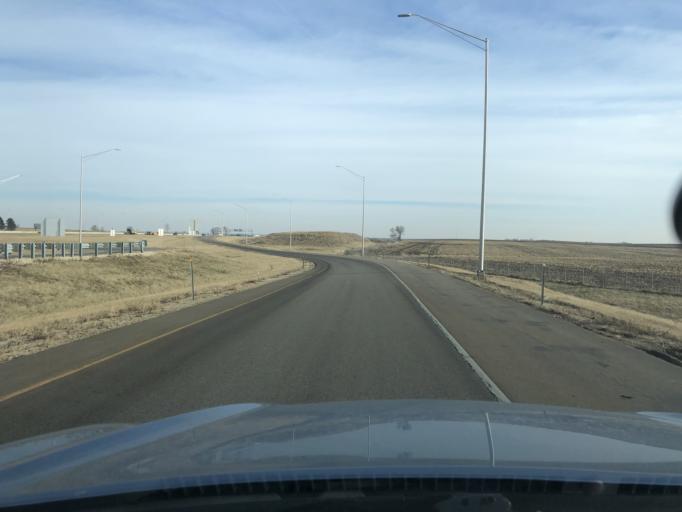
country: US
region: Illinois
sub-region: Boone County
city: Belvidere
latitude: 42.2317
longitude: -88.8159
